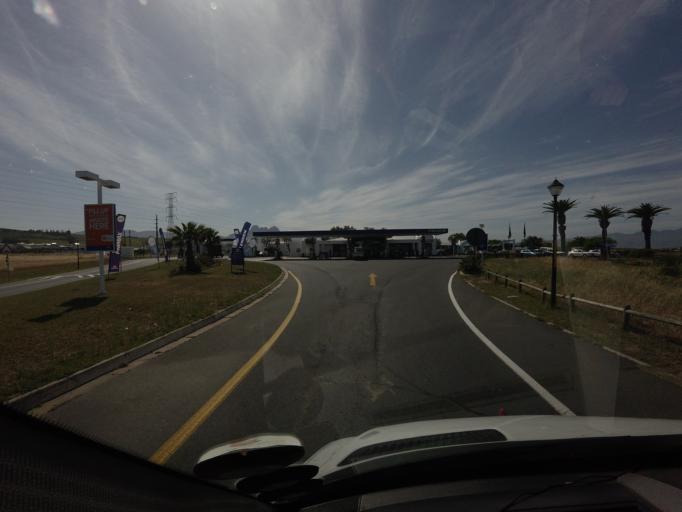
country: ZA
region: Western Cape
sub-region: Cape Winelands District Municipality
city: Stellenbosch
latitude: -34.0473
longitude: 18.7565
